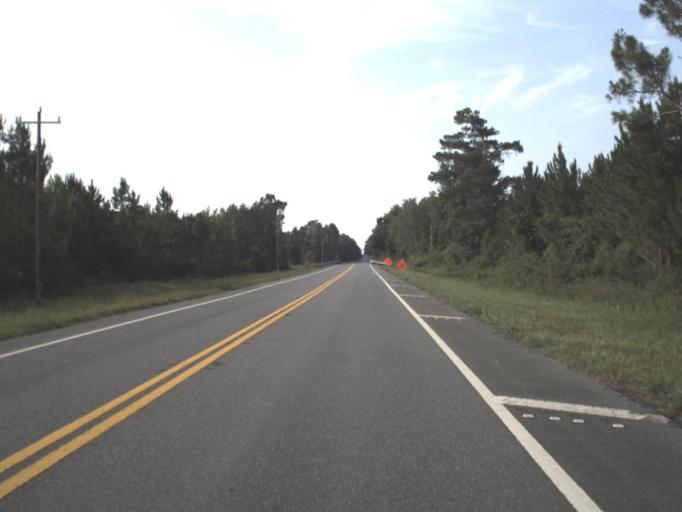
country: US
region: Florida
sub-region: Taylor County
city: Perry
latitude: 30.2016
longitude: -83.6068
